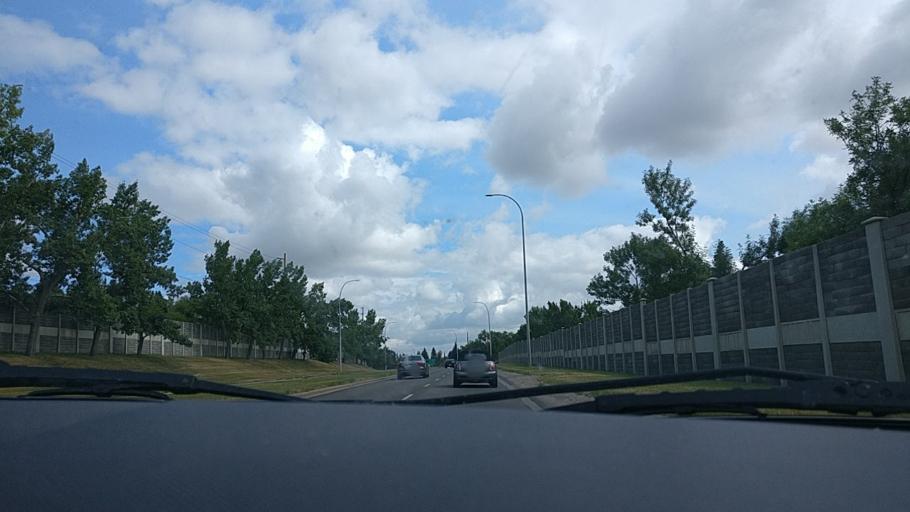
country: CA
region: Alberta
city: Calgary
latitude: 51.0940
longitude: -114.0861
